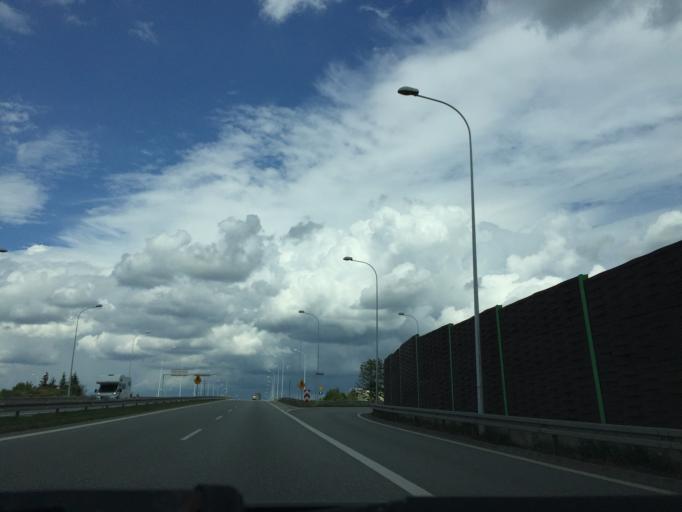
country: PL
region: Swietokrzyskie
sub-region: Powiat skarzyski
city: Skarzysko-Kamienna
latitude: 51.1013
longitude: 20.8363
